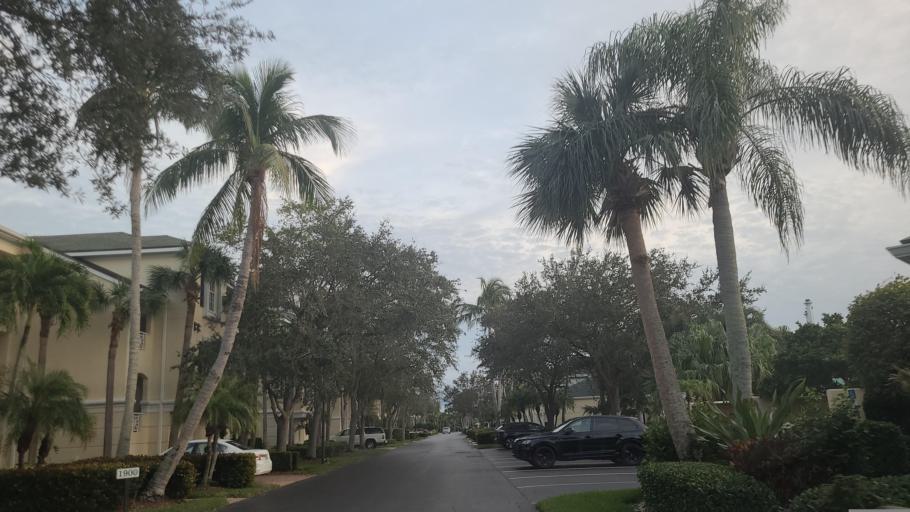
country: US
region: Florida
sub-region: Indian River County
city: Vero Beach
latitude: 27.6372
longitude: -80.3763
